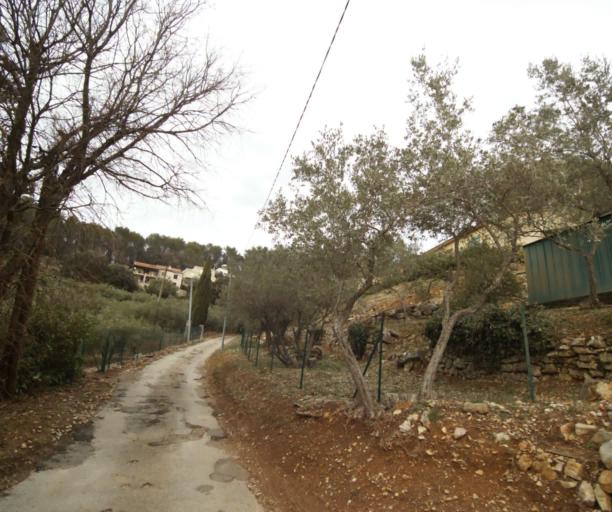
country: FR
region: Provence-Alpes-Cote d'Azur
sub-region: Departement du Var
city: Trans-en-Provence
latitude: 43.5097
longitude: 6.4860
